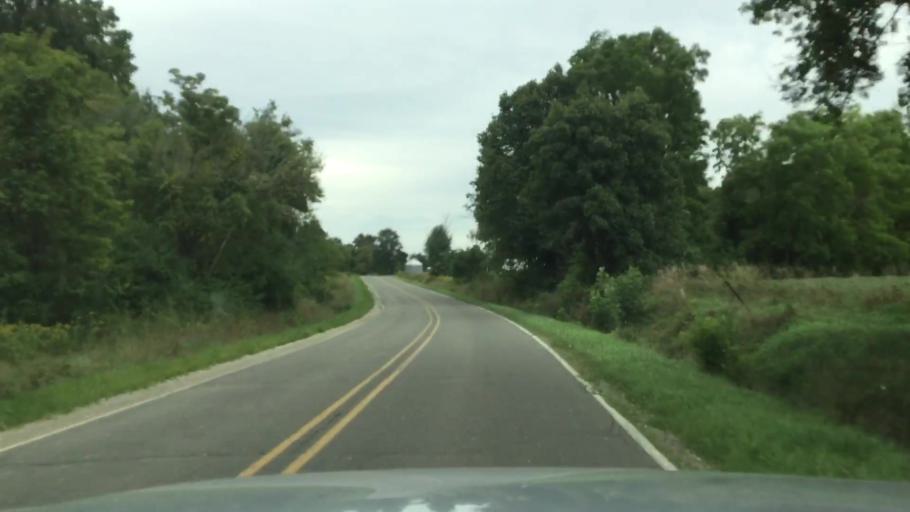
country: US
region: Michigan
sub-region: Shiawassee County
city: Durand
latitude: 42.8480
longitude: -84.0365
